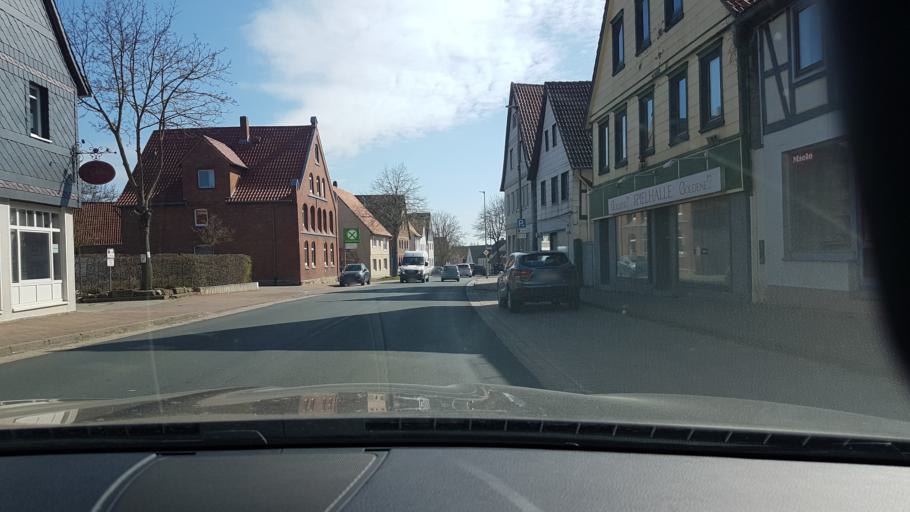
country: DE
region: Lower Saxony
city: Elze
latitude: 52.1837
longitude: 9.6724
